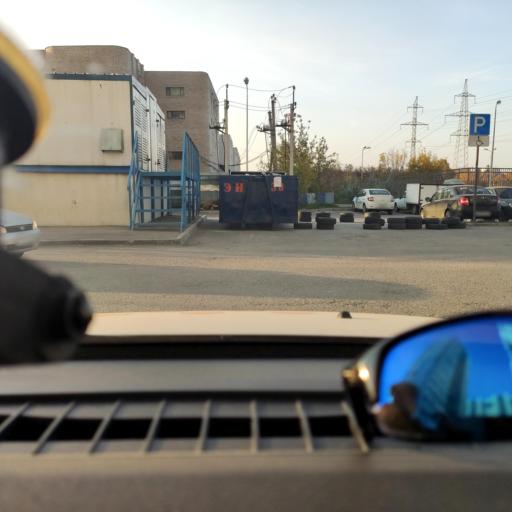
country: RU
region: Samara
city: Samara
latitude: 53.2666
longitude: 50.2319
